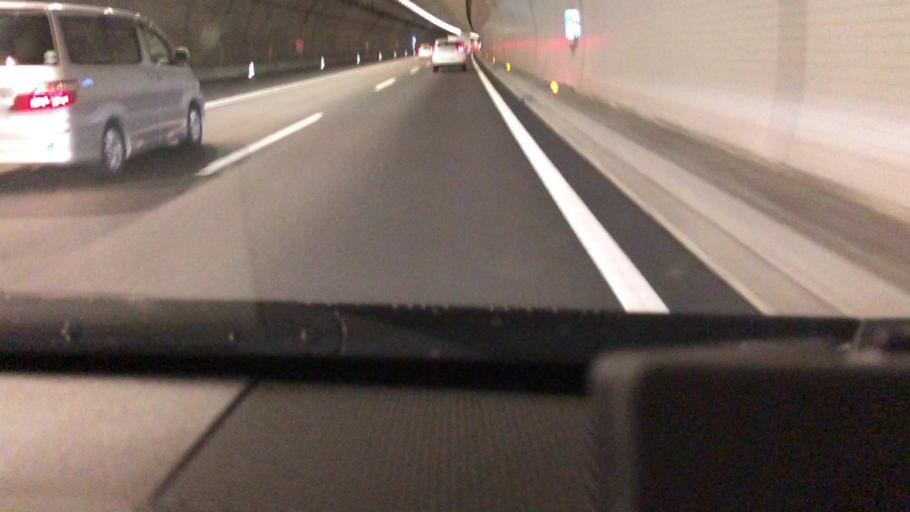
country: JP
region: Shizuoka
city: Shimada
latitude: 34.8780
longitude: 138.1850
